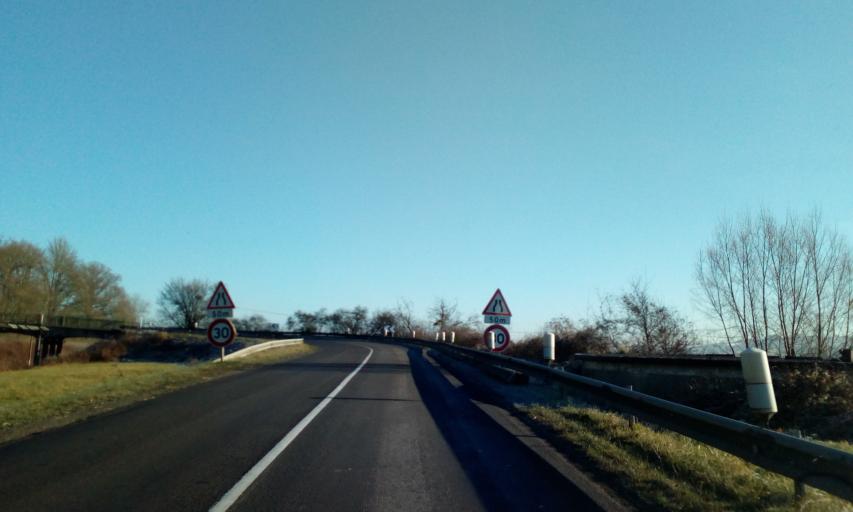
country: FR
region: Champagne-Ardenne
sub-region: Departement des Ardennes
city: Rimogne
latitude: 49.7970
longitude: 4.5100
